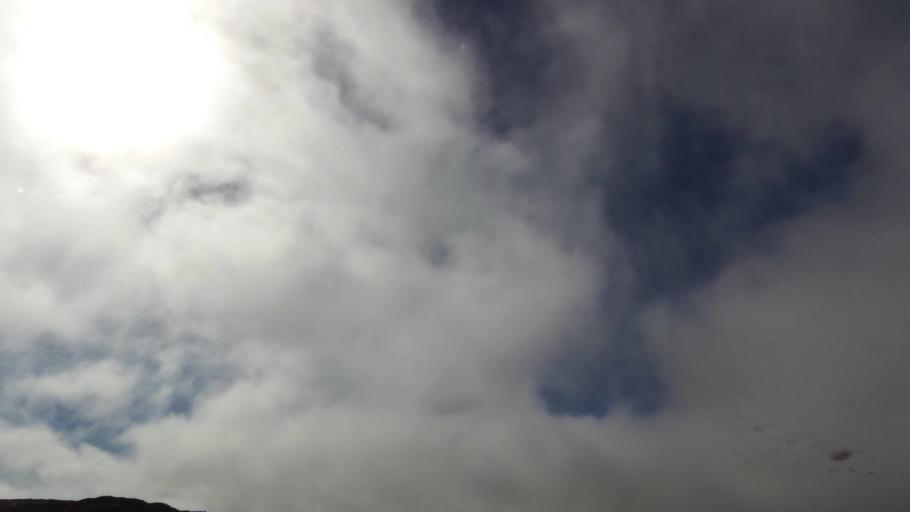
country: IS
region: West
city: Olafsvik
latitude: 65.5578
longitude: -24.2406
